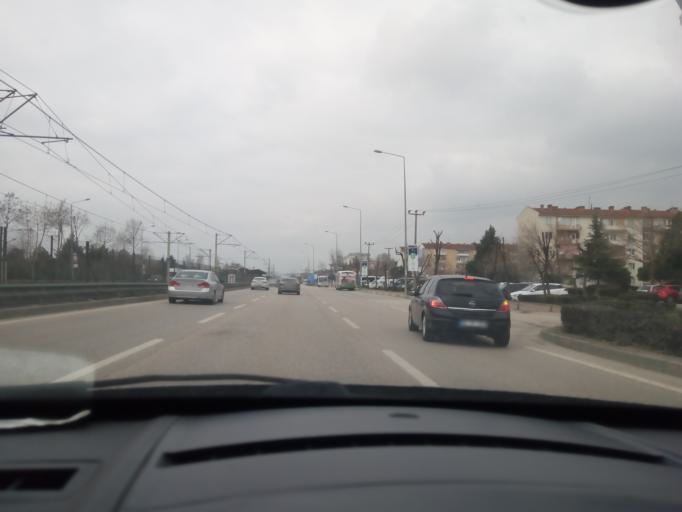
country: TR
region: Bursa
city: Niluefer
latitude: 40.2424
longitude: 28.9687
